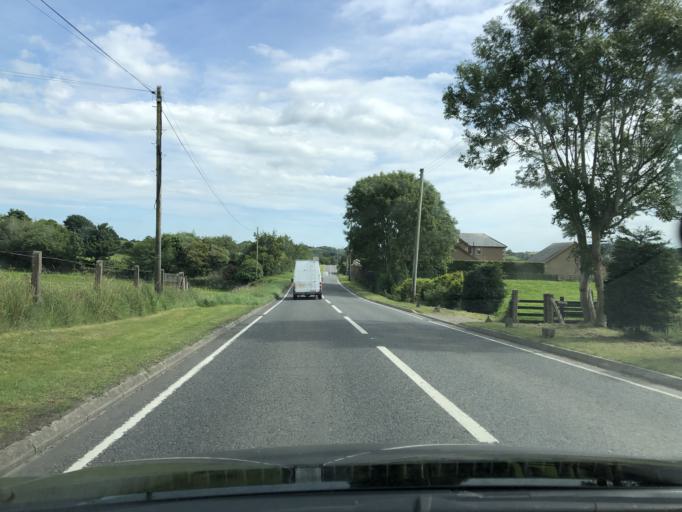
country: GB
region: Northern Ireland
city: Ballynahinch
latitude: 54.4224
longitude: -5.9185
